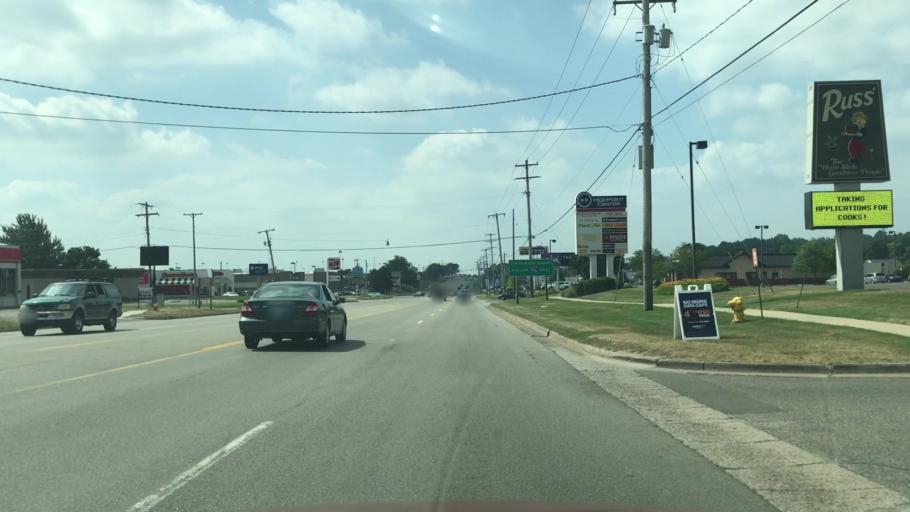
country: US
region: Michigan
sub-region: Kent County
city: Comstock Park
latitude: 43.0281
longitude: -85.6894
